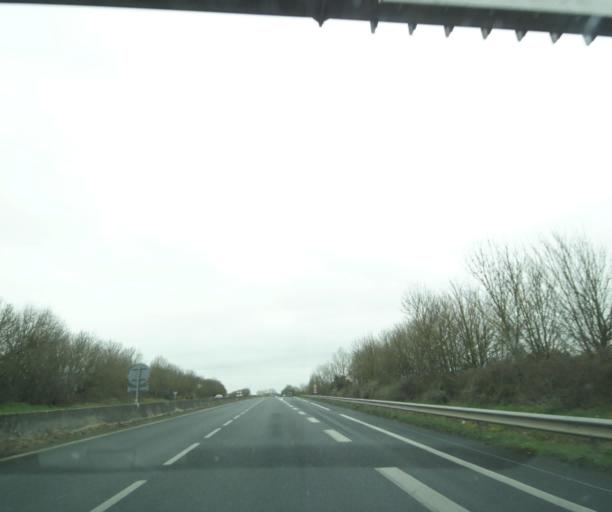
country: FR
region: Poitou-Charentes
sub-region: Departement de la Charente-Maritime
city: Breuil-Magne
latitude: 45.9657
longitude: -0.9731
